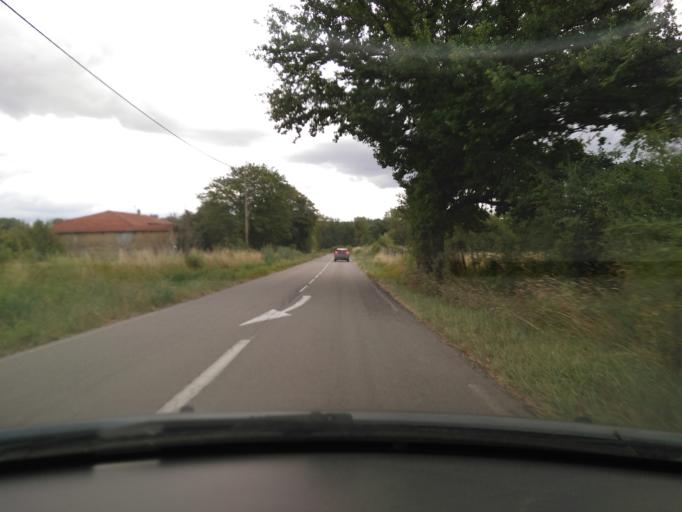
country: FR
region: Rhone-Alpes
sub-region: Departement de l'Isere
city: Beaurepaire
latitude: 45.4012
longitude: 5.1318
